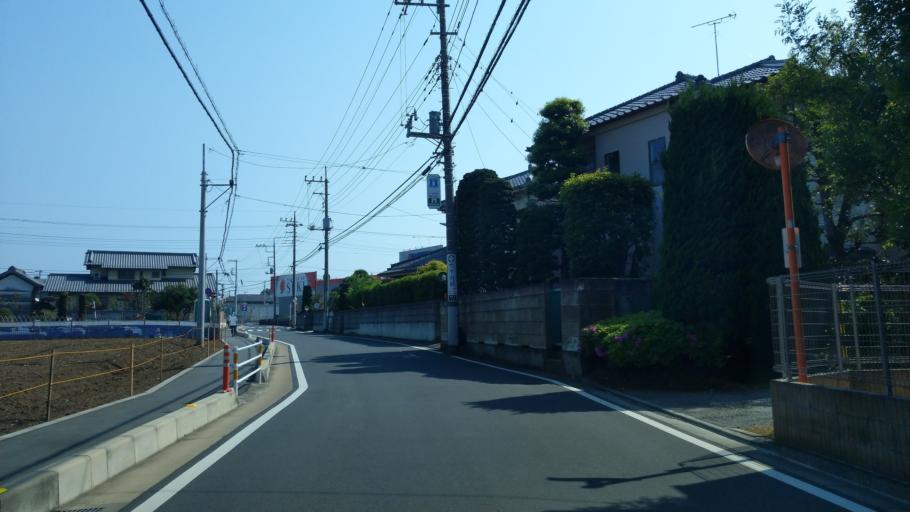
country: JP
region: Saitama
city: Kamifukuoka
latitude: 35.8698
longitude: 139.5282
